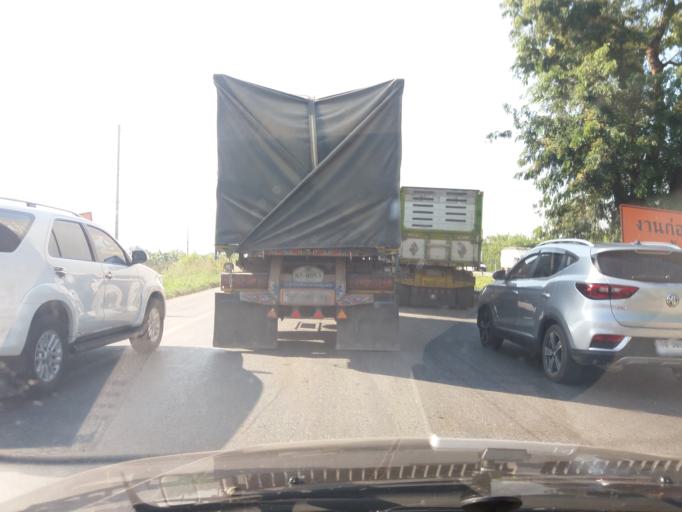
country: TH
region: Nakhon Sawan
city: Nakhon Sawan
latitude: 15.7360
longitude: 100.0236
